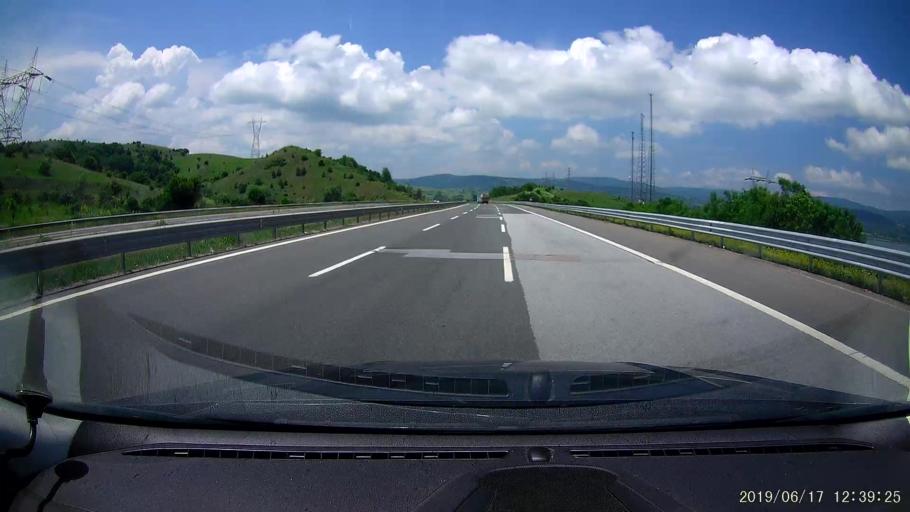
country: TR
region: Bolu
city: Yenicaga
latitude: 40.7656
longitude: 32.0369
